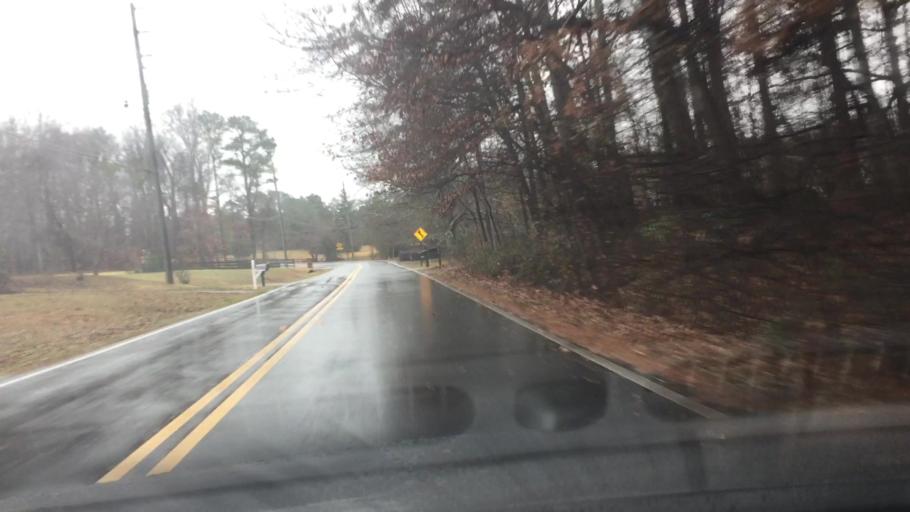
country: US
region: Georgia
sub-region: Cobb County
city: Kennesaw
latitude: 33.9693
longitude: -84.6340
